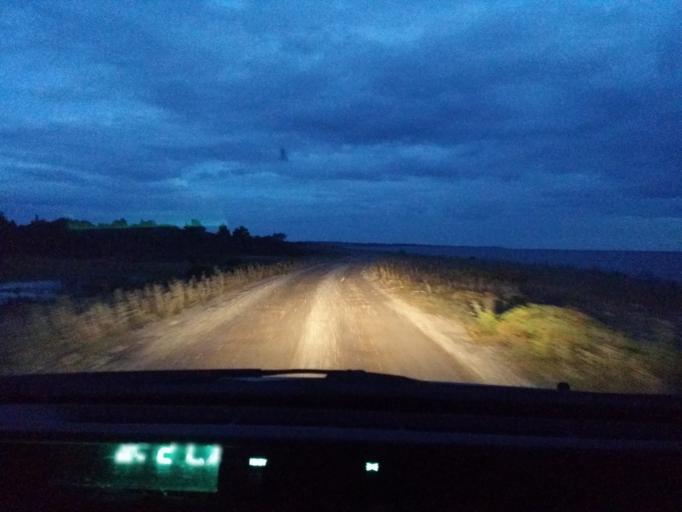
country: SE
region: Kalmar
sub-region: Borgholms Kommun
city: Borgholm
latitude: 57.1334
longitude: 16.9019
